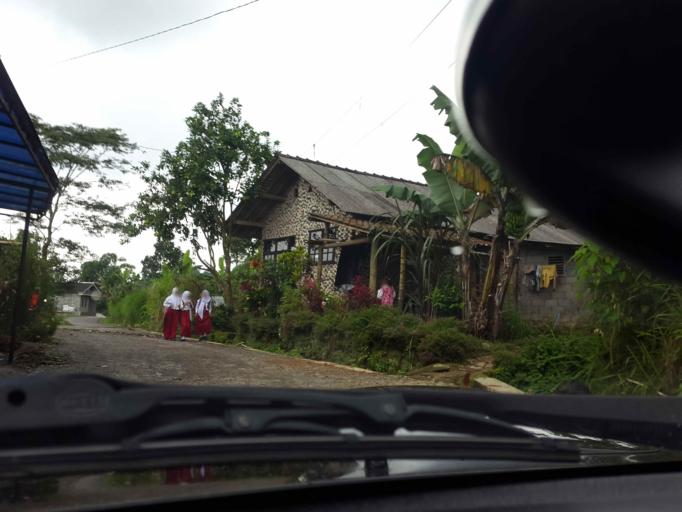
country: ID
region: Central Java
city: Wonosobo
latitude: -7.3633
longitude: 109.9624
